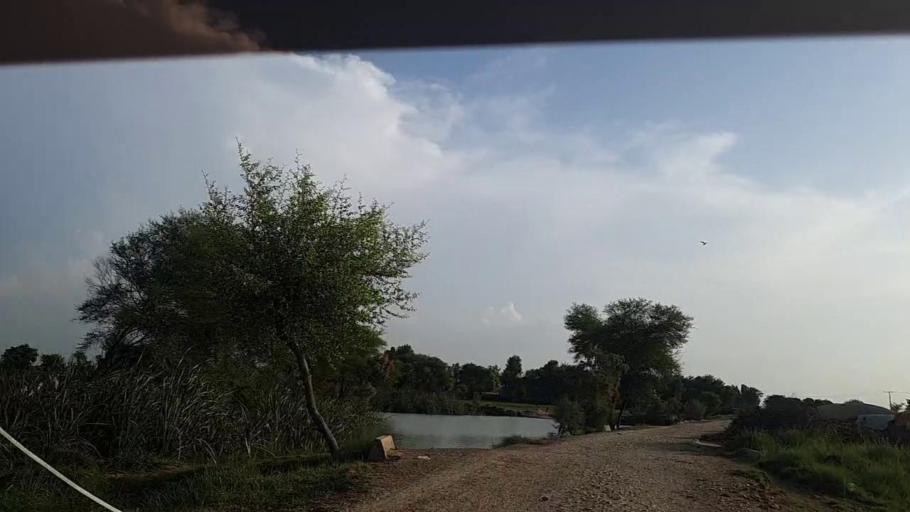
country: PK
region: Sindh
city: Khanpur
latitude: 27.8083
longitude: 69.3377
